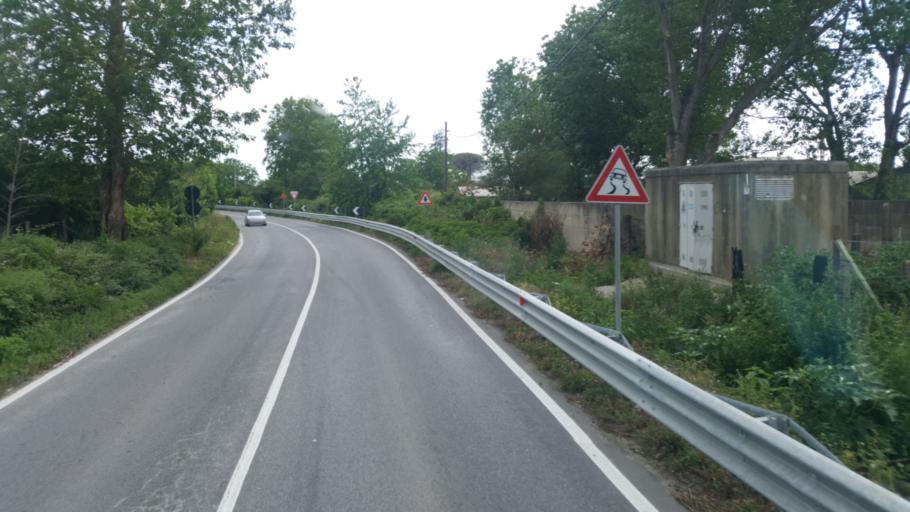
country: IT
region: Campania
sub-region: Provincia di Napoli
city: Acerra
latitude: 40.9754
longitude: 14.3922
